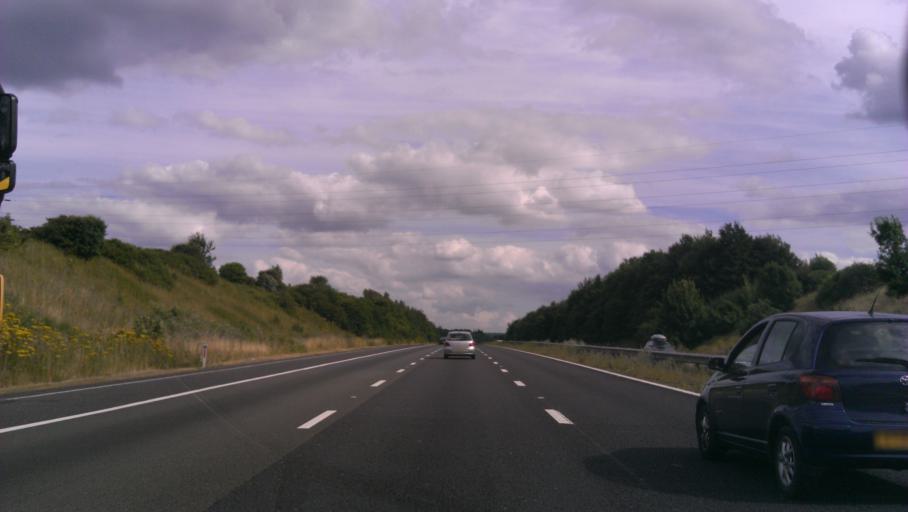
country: GB
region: England
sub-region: Kent
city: Eynsford
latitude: 51.3686
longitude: 0.2574
